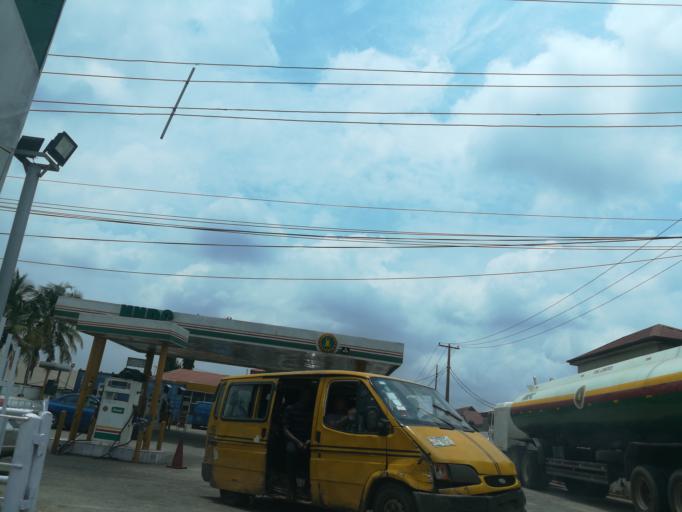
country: NG
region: Lagos
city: Ojota
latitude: 6.5931
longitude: 3.3717
